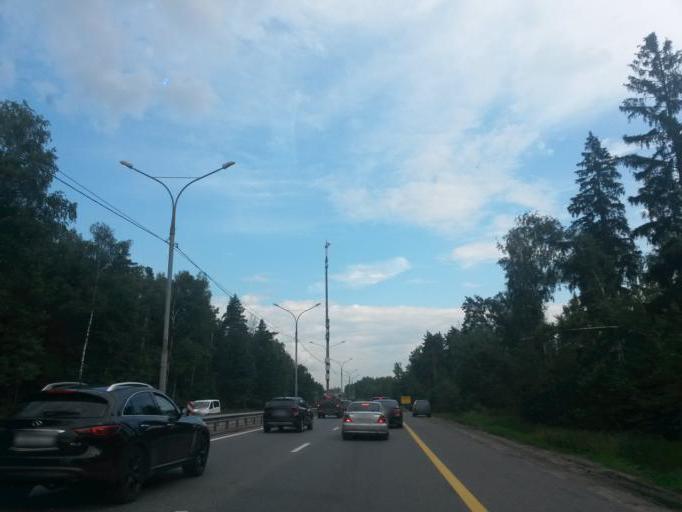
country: RU
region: Moskovskaya
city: Vostryakovo
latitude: 55.4449
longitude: 37.8640
